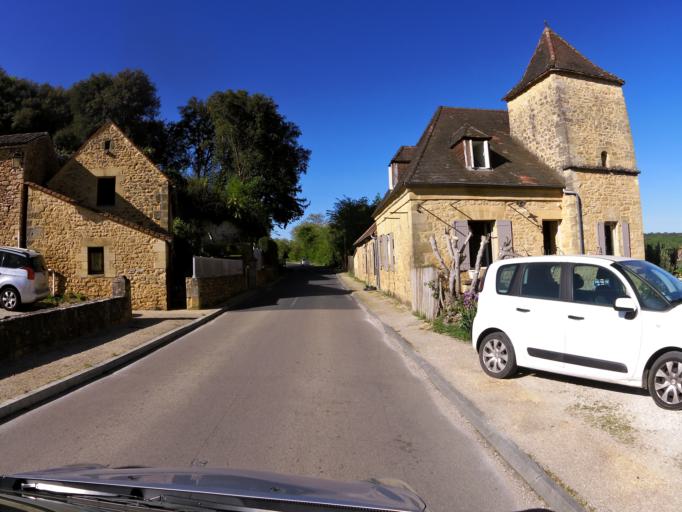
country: FR
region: Aquitaine
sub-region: Departement de la Dordogne
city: Carsac-Aillac
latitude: 44.8384
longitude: 1.2487
